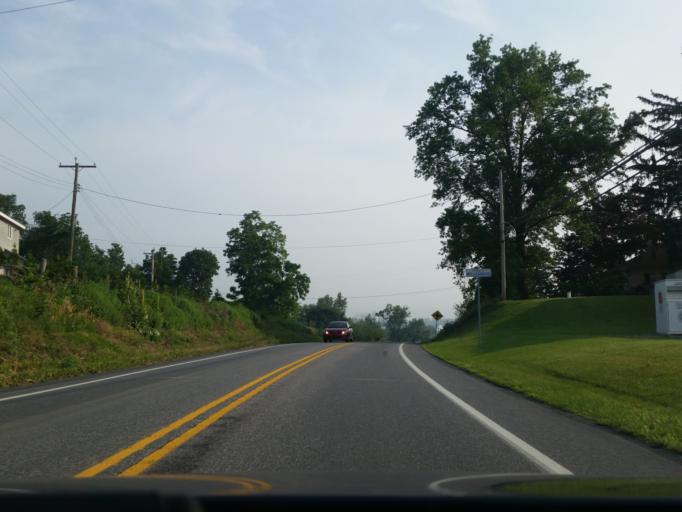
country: US
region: Pennsylvania
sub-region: Lebanon County
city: Annville
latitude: 40.3589
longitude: -76.5474
